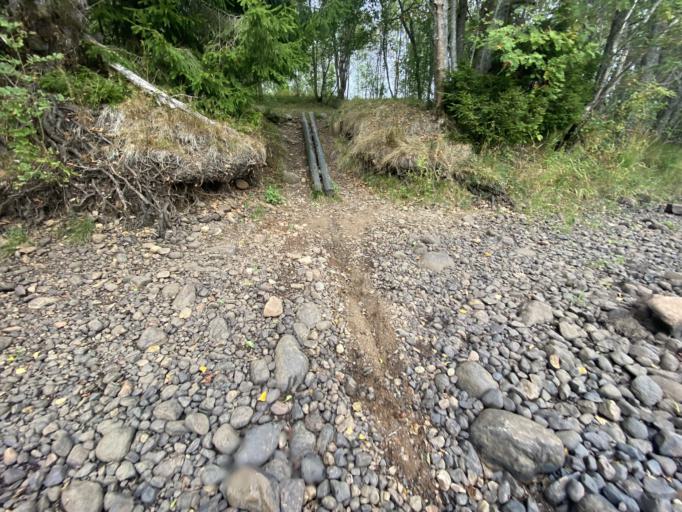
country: SE
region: Kronoberg
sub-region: Markaryds Kommun
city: Markaryd
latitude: 56.4857
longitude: 13.5995
